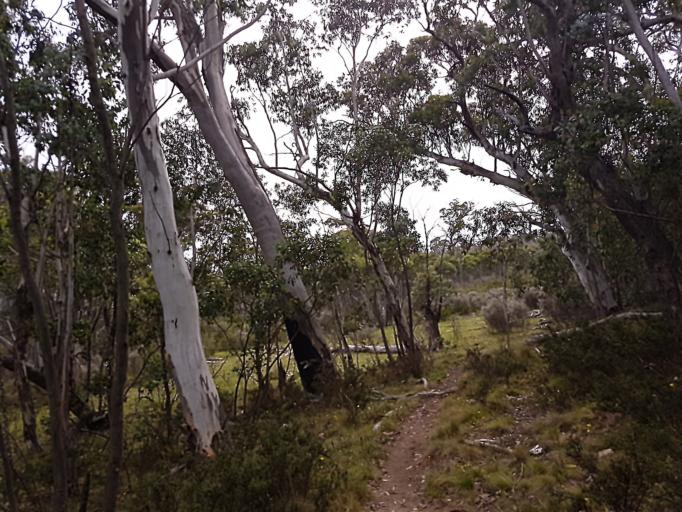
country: AU
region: New South Wales
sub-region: Snowy River
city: Jindabyne
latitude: -36.8047
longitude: 148.1855
